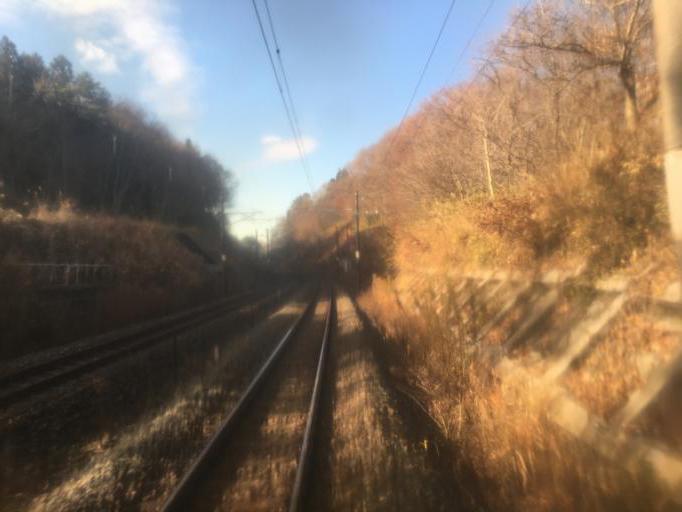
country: JP
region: Miyagi
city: Kogota
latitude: 38.6808
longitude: 141.0815
